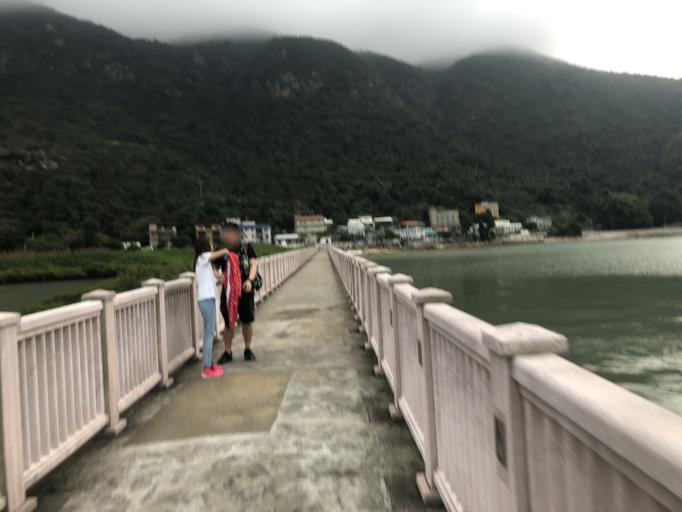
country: HK
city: Tai O
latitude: 22.2484
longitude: 113.8611
